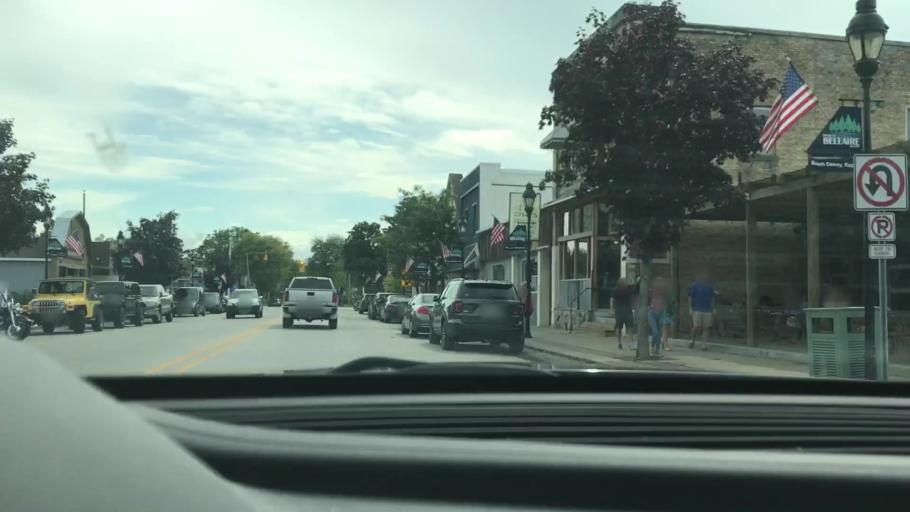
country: US
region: Michigan
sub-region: Antrim County
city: Bellaire
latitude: 44.9765
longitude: -85.2100
